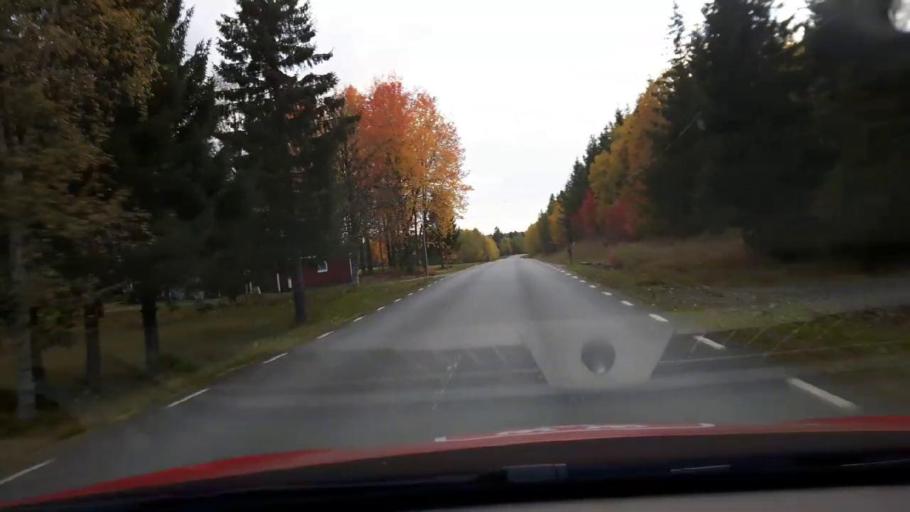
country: SE
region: Jaemtland
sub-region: OEstersunds Kommun
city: Lit
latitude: 63.3276
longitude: 15.1757
